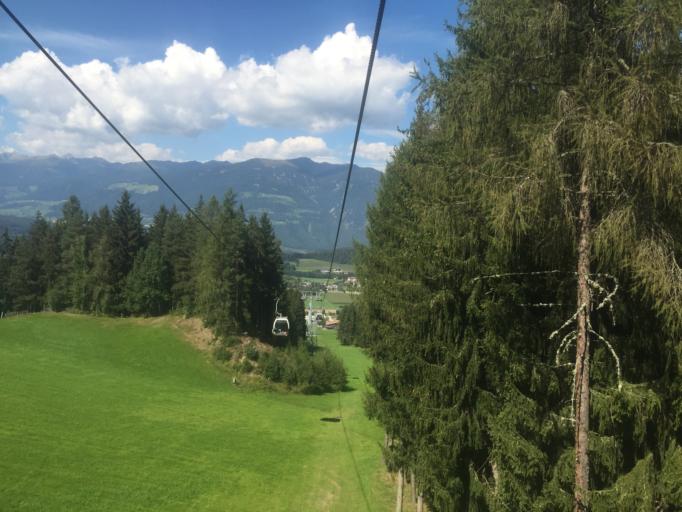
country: IT
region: Trentino-Alto Adige
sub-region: Bolzano
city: Riscone
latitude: 46.7645
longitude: 11.9447
